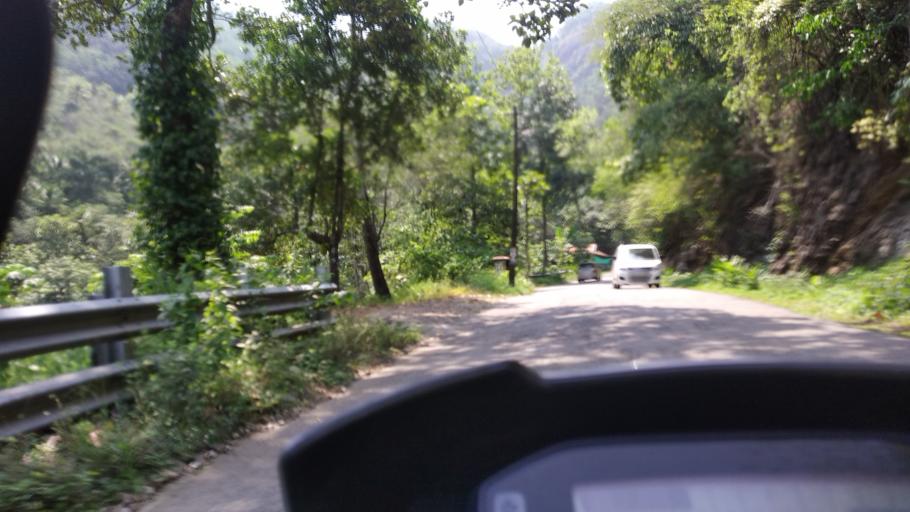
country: IN
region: Kerala
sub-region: Kottayam
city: Erattupetta
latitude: 9.6928
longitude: 76.8697
